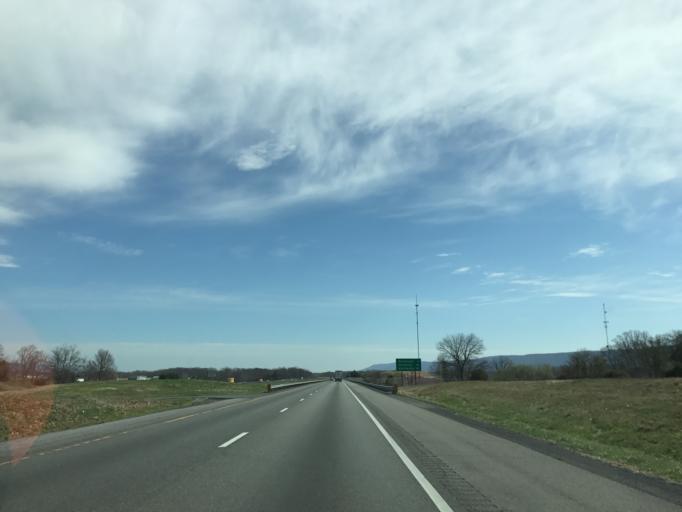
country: US
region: Virginia
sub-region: Shenandoah County
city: Edinburg
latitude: 38.8384
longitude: -78.5638
